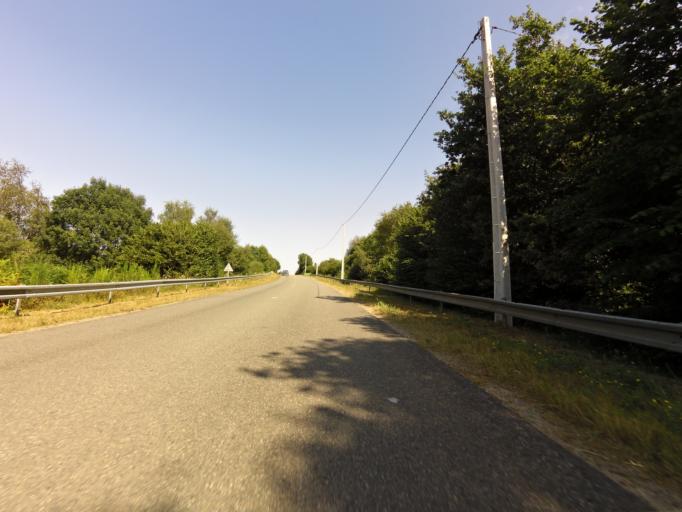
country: FR
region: Brittany
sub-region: Departement du Morbihan
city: Questembert
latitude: 47.6594
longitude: -2.4299
